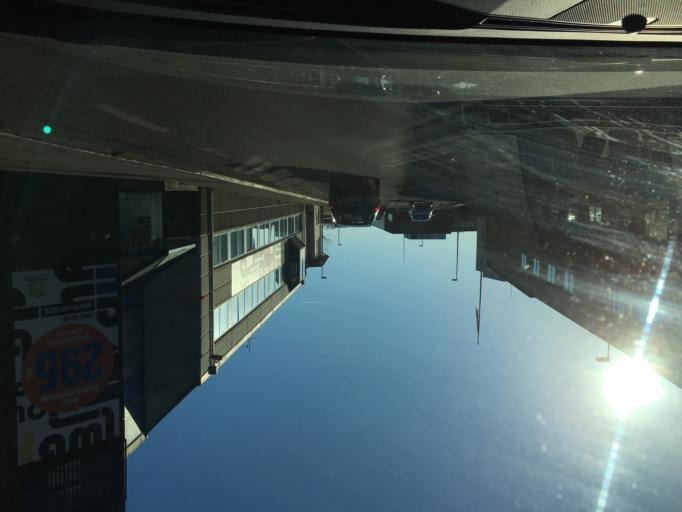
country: DK
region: South Denmark
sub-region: Kolding Kommune
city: Kolding
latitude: 55.4898
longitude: 9.4782
